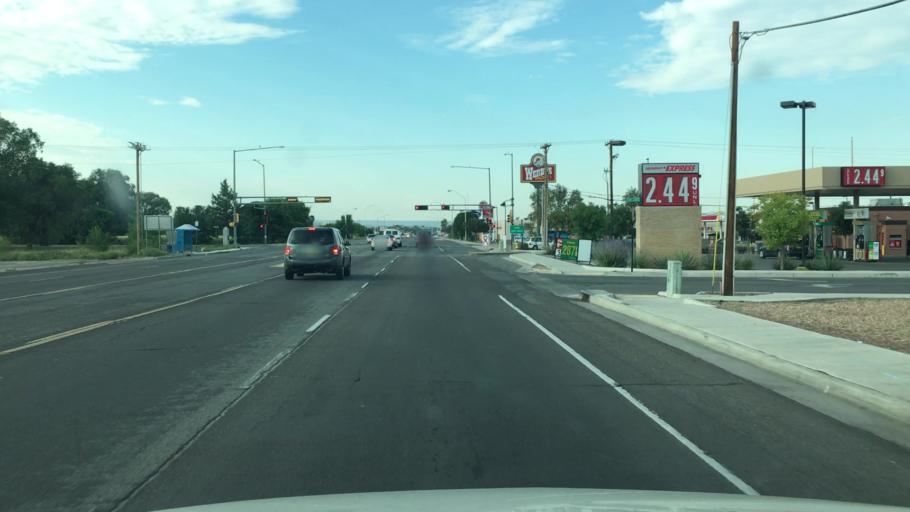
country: US
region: New Mexico
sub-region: Rio Arriba County
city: Espanola
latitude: 36.0170
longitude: -106.0645
